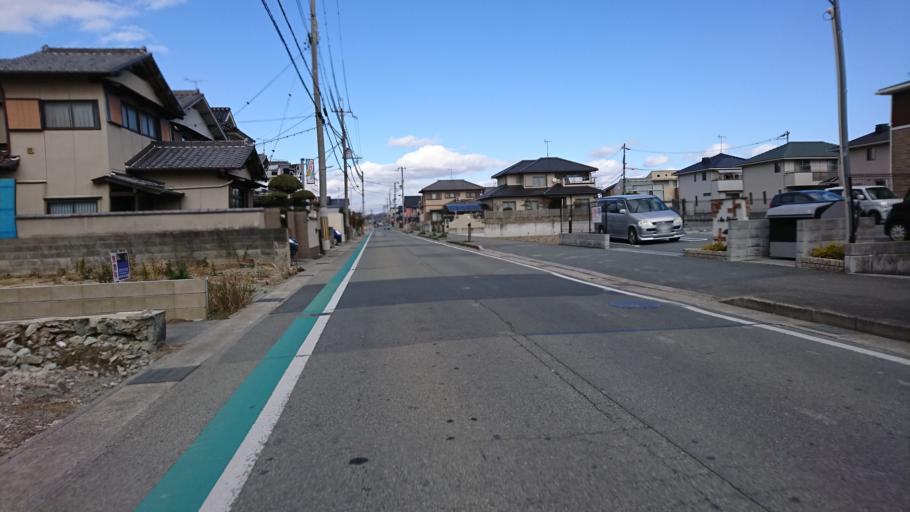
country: JP
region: Hyogo
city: Kakogawacho-honmachi
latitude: 34.7763
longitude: 134.8009
